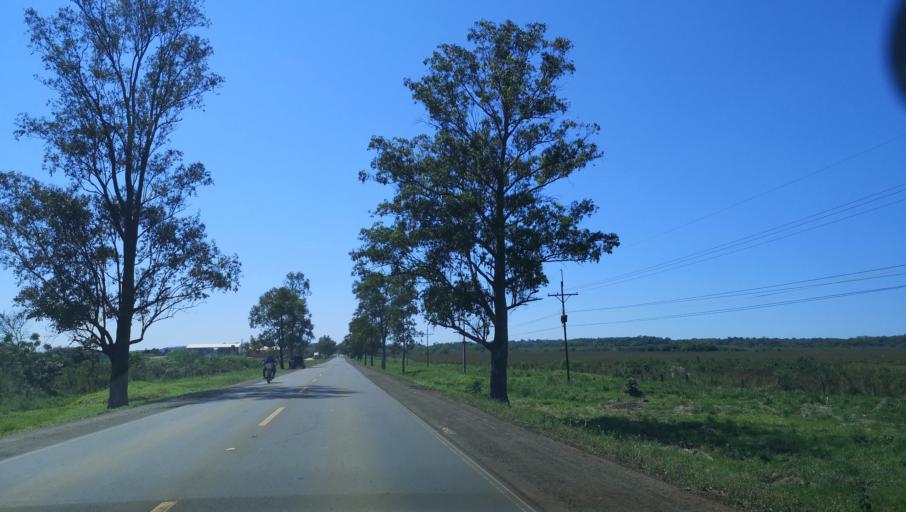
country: PY
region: Itapua
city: Carmen del Parana
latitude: -27.2207
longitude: -56.1287
